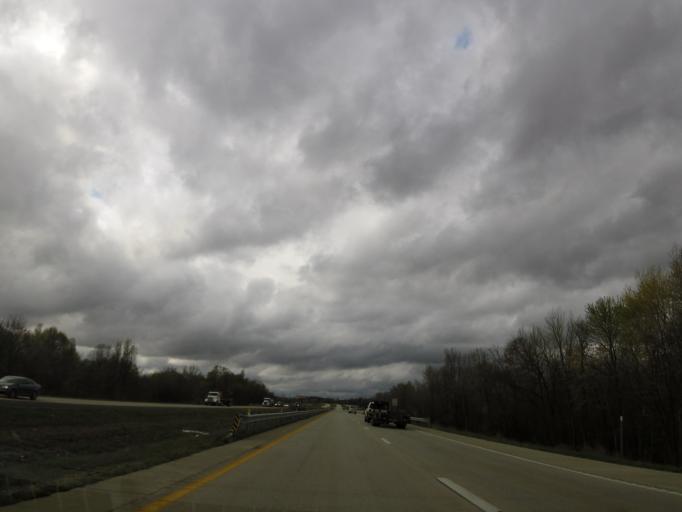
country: US
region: Missouri
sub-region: Butler County
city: Poplar Bluff
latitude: 36.6951
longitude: -90.4783
